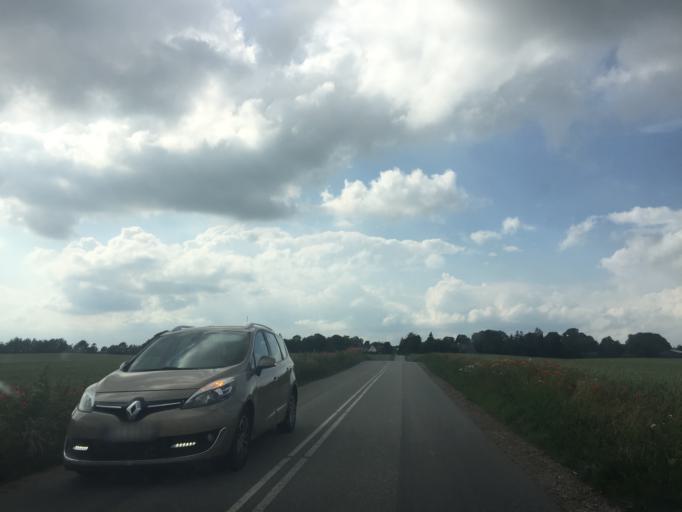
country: DK
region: Capital Region
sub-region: Hoje-Taastrup Kommune
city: Flong
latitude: 55.6896
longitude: 12.1725
